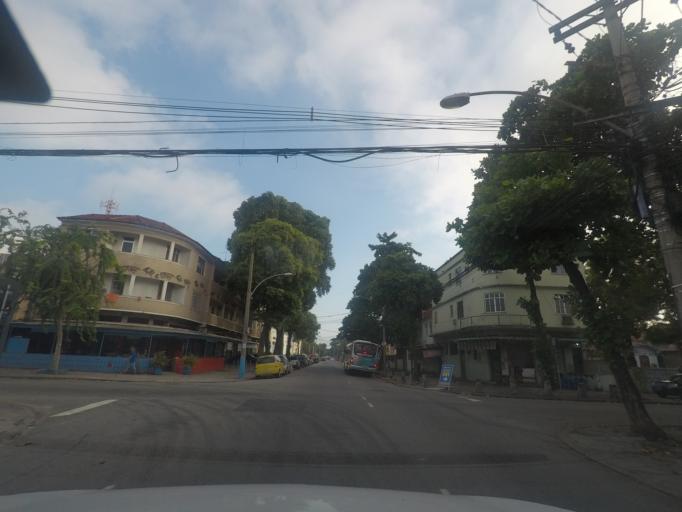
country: BR
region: Rio de Janeiro
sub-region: Duque De Caxias
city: Duque de Caxias
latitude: -22.8318
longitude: -43.2759
